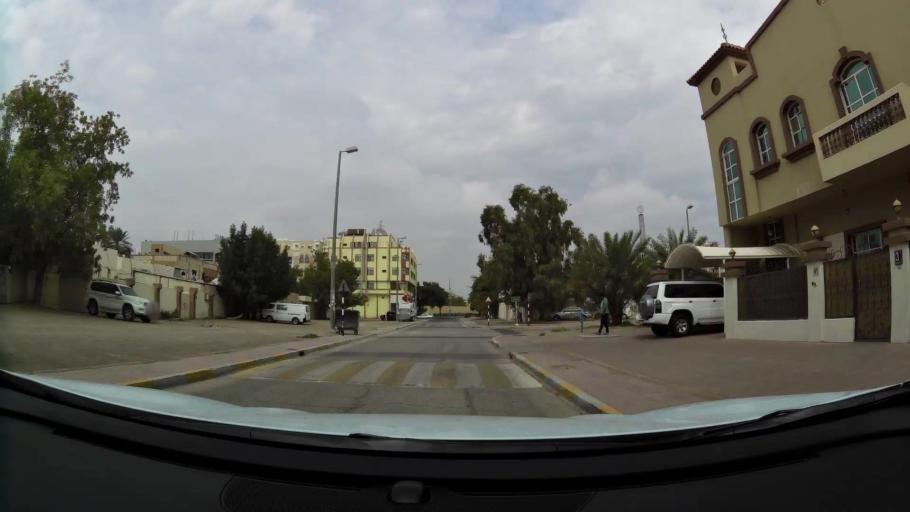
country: AE
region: Abu Dhabi
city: Al Ain
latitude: 24.2199
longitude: 55.7786
